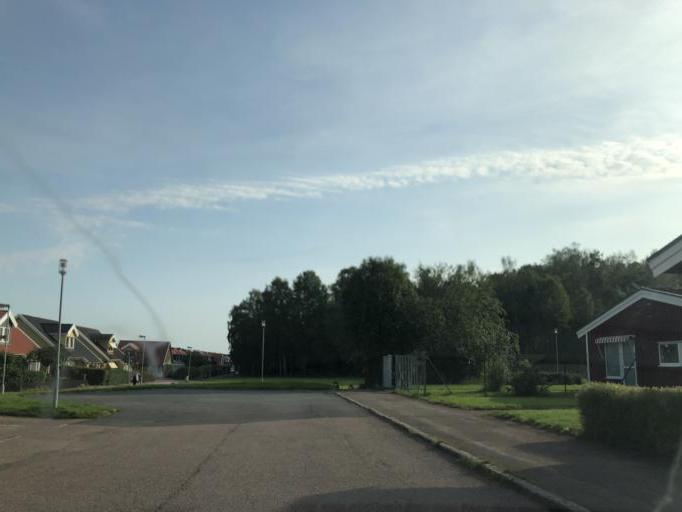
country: SE
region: Vaestra Goetaland
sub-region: Goteborg
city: Goeteborg
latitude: 57.7464
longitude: 11.9843
